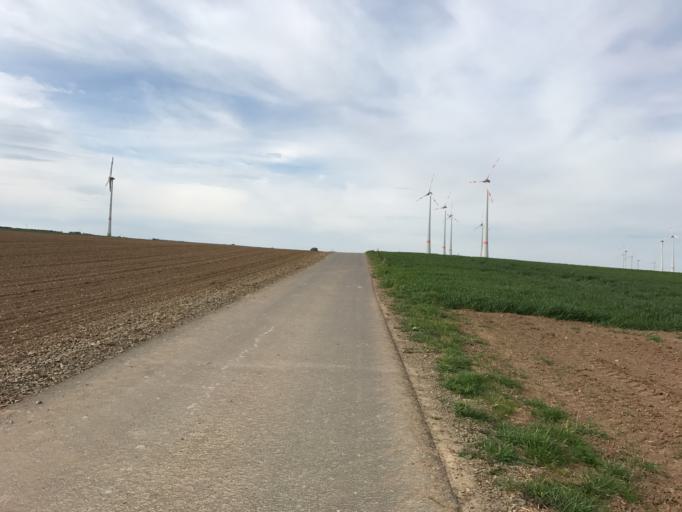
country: DE
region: Rheinland-Pfalz
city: Spiesheim
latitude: 49.8176
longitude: 8.1395
